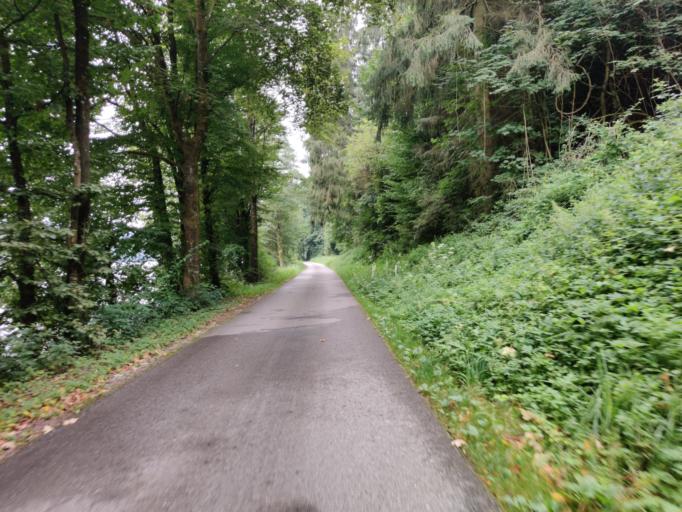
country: AT
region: Lower Austria
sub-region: Politischer Bezirk Melk
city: Nochling
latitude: 48.2154
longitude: 14.9507
